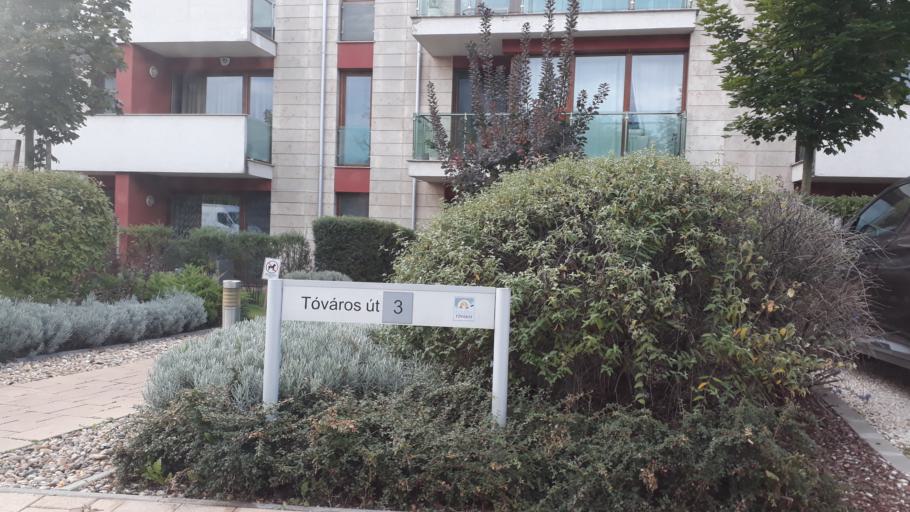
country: HU
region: Pest
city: Budaors
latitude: 47.4481
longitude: 18.9972
